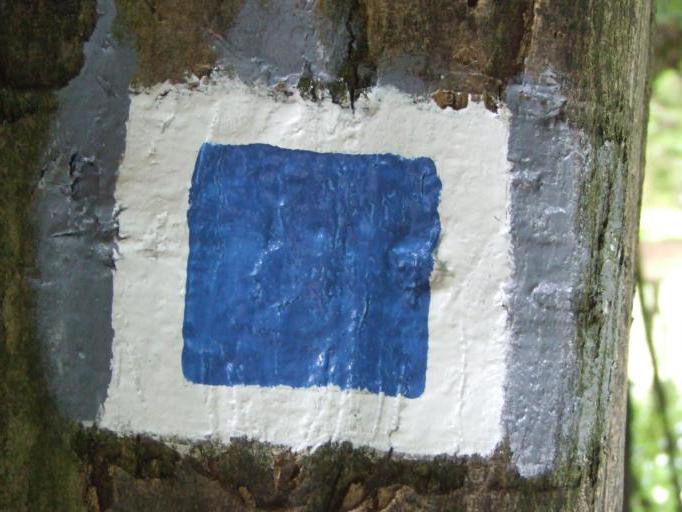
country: HU
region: Somogy
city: Kaposvar
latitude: 46.3291
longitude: 17.7961
